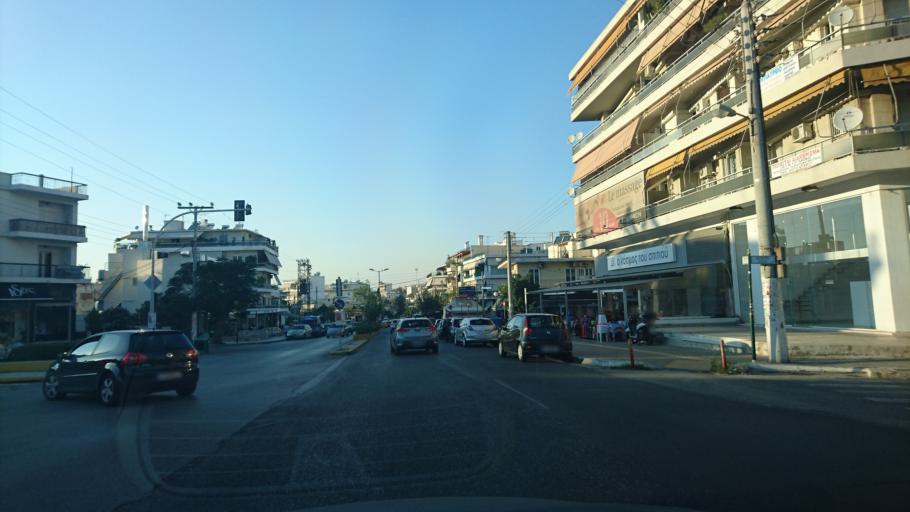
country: GR
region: Attica
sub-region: Nomarchia Athinas
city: Ilioupoli
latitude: 37.9386
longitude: 23.7569
